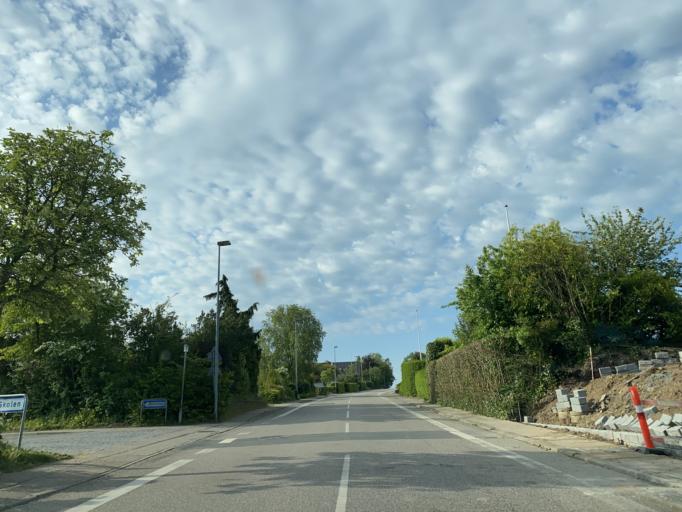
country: DK
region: South Denmark
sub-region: Sonderborg Kommune
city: Dybbol
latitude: 54.9115
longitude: 9.7655
